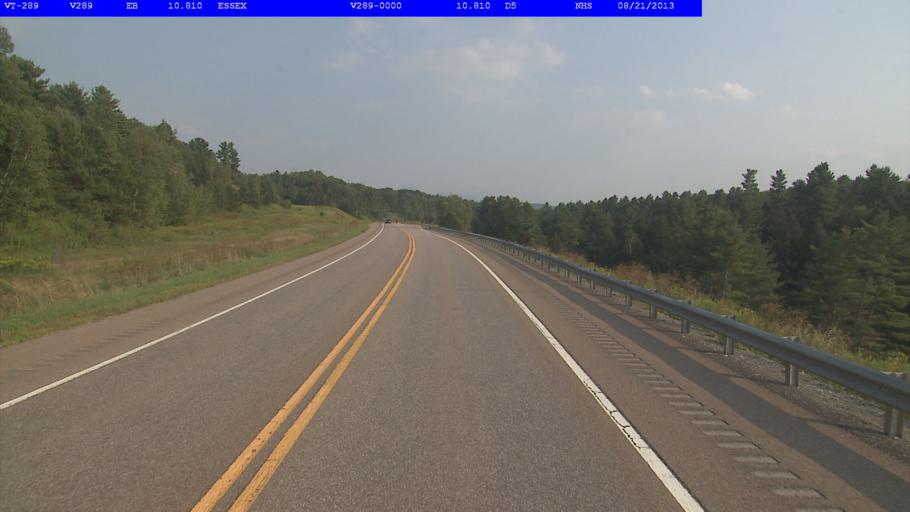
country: US
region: Vermont
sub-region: Chittenden County
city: Essex Junction
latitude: 44.4957
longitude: -73.0684
